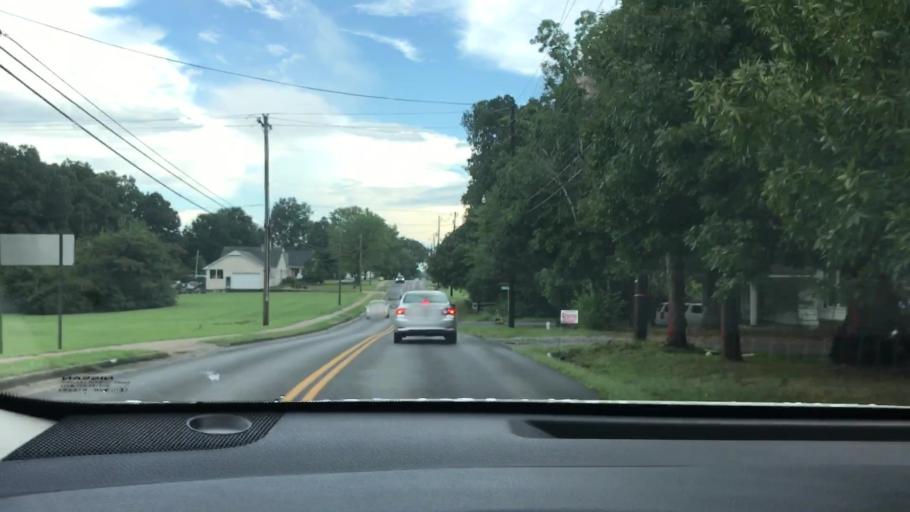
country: US
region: Kentucky
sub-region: Calloway County
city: Murray
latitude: 36.6059
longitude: -88.3245
